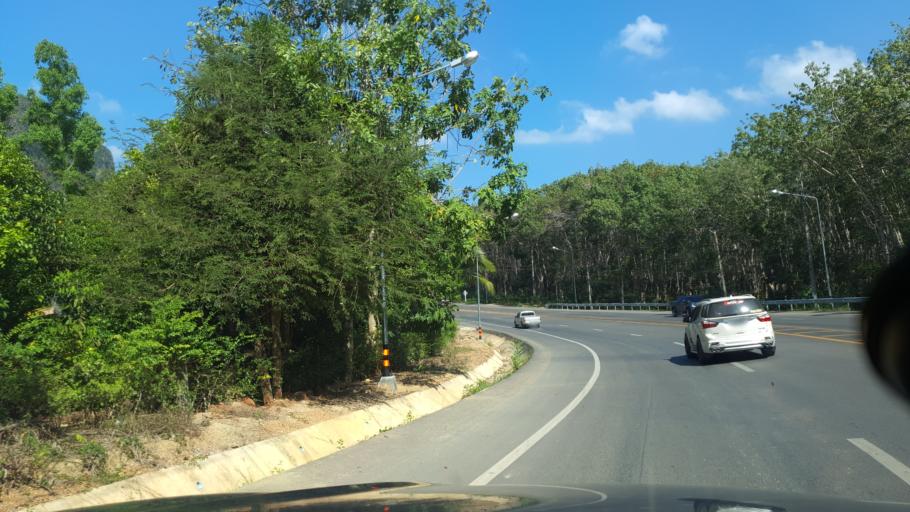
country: TH
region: Krabi
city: Krabi
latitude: 8.0749
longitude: 98.8583
